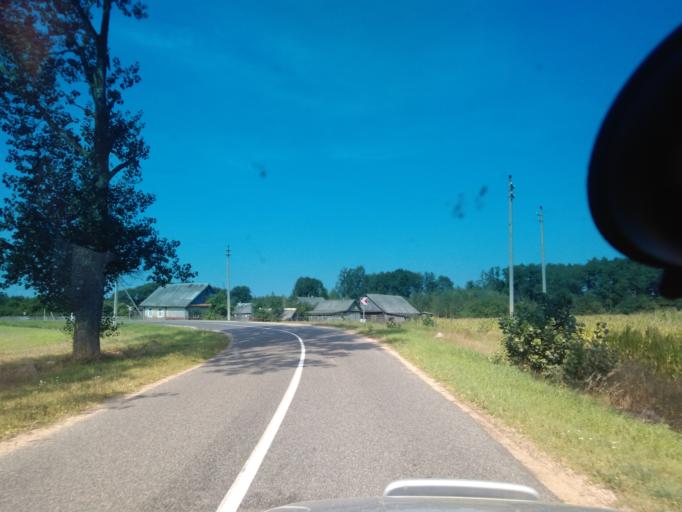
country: BY
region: Minsk
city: Kapyl'
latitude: 53.2732
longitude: 27.2094
